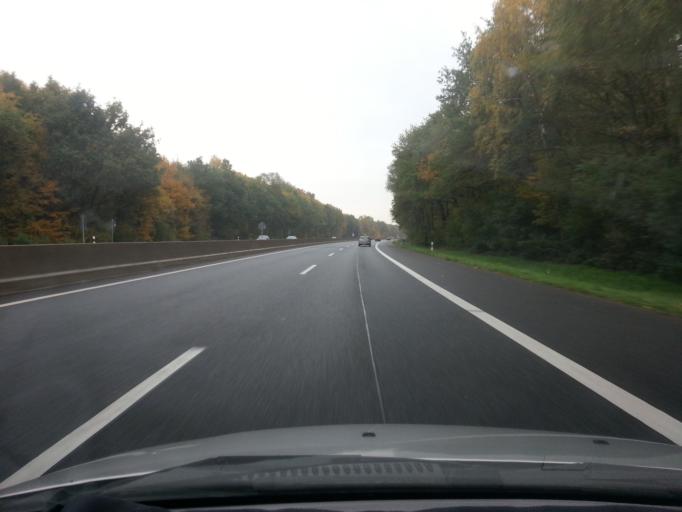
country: DE
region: Hesse
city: Dreieich
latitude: 50.0005
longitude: 8.6908
